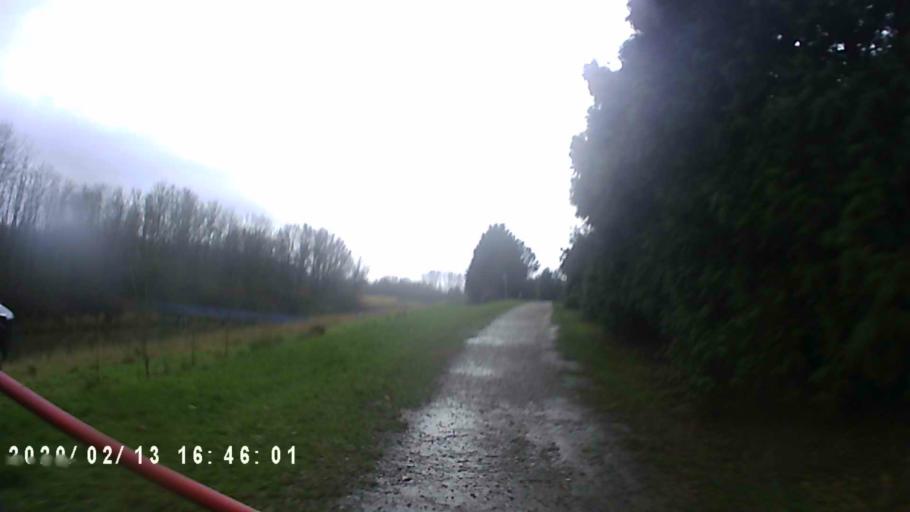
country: NL
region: Groningen
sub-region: Gemeente Groningen
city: Groningen
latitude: 53.2195
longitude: 6.5207
